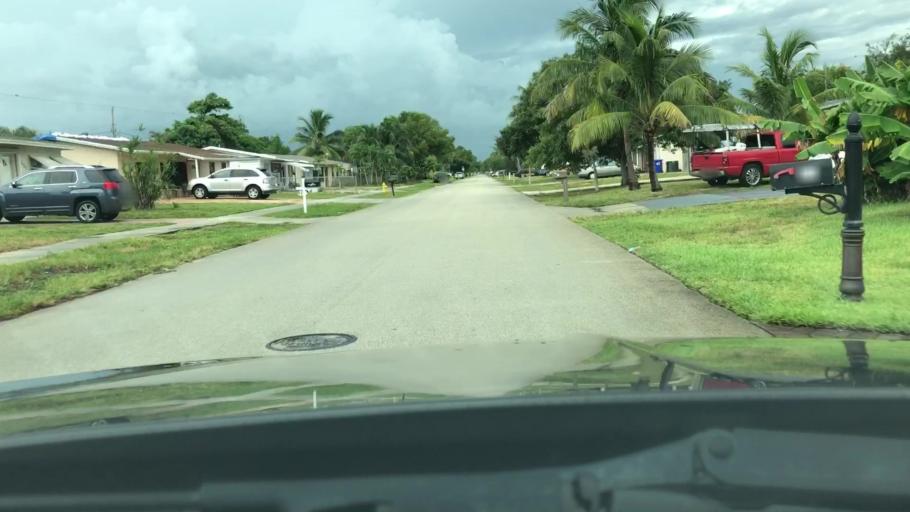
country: US
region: Florida
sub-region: Broward County
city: Pompano Beach Highlands
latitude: 26.2705
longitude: -80.1081
